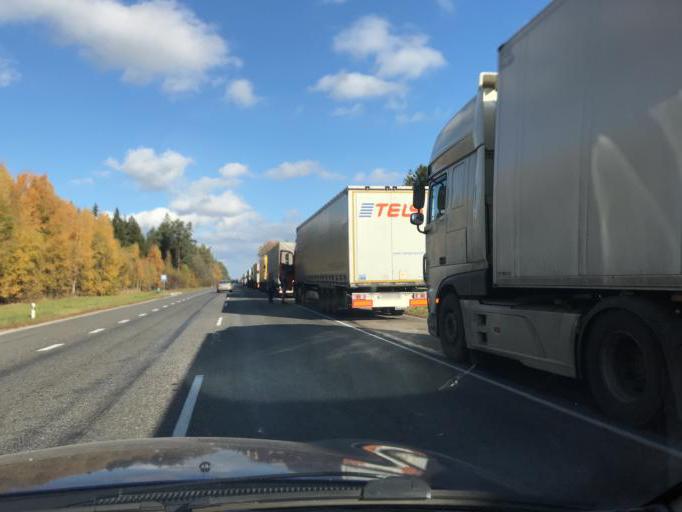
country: BY
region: Grodnenskaya
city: Voranava
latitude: 54.2198
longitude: 25.3549
